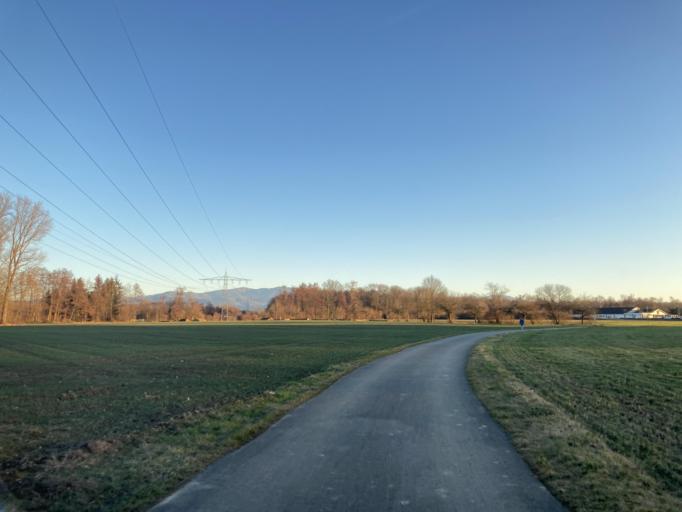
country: DE
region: Baden-Wuerttemberg
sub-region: Freiburg Region
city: Umkirch
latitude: 48.0479
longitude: 7.7687
